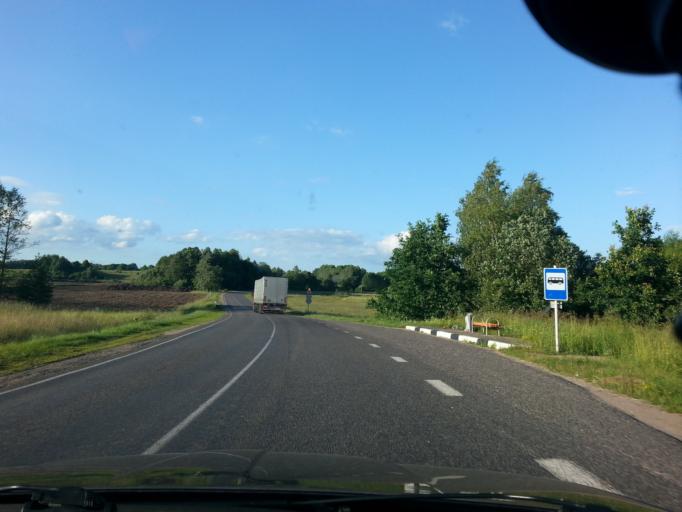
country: BY
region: Minsk
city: Svir
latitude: 54.8593
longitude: 26.3193
